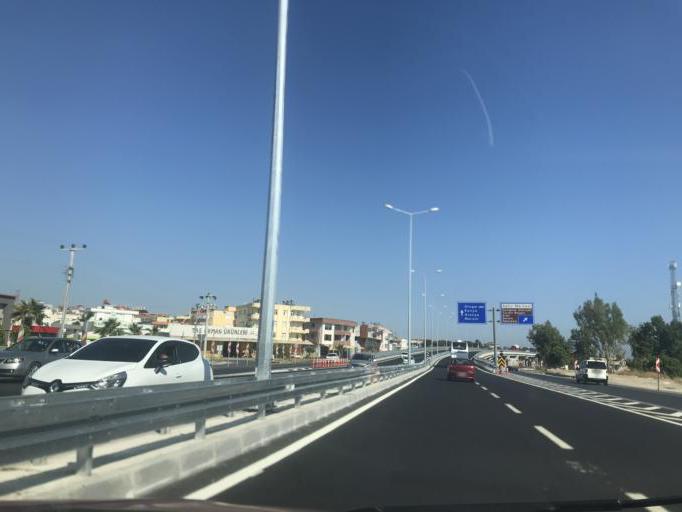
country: TR
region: Antalya
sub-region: Manavgat
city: Manavgat
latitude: 36.7968
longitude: 31.4085
